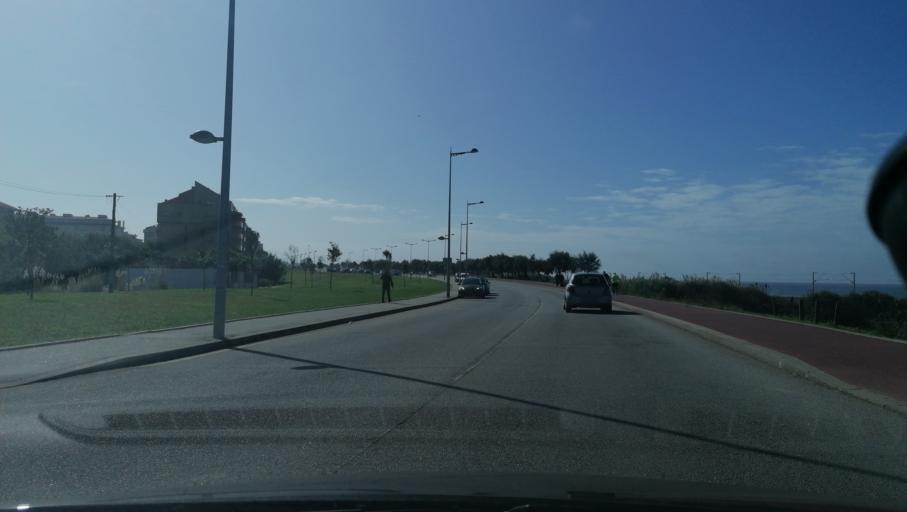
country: PT
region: Aveiro
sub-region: Espinho
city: Espinho
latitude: 41.0265
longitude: -8.6429
